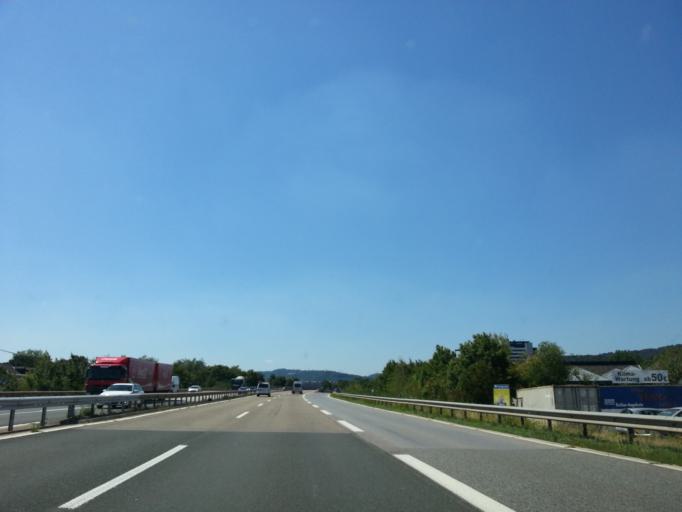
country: DE
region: Rheinland-Pfalz
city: Trier
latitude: 49.7738
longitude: 6.6714
